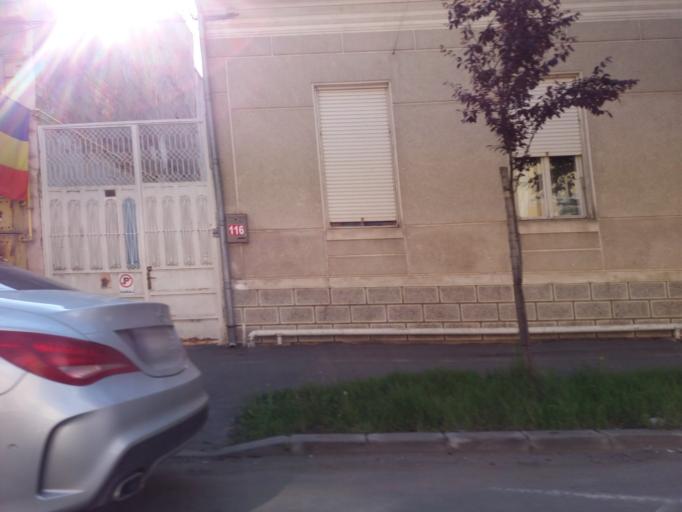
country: RO
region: Arad
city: Arad
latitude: 46.1728
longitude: 21.3051
